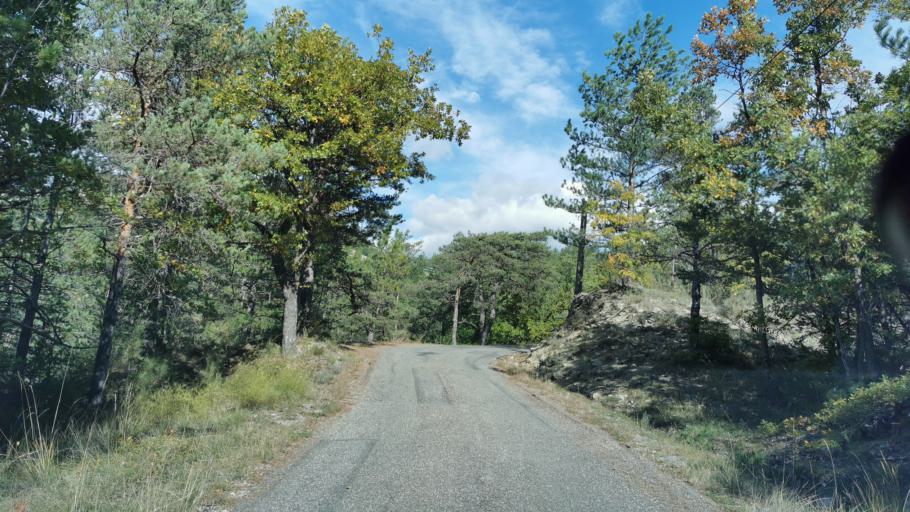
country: FR
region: Provence-Alpes-Cote d'Azur
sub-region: Departement des Alpes-de-Haute-Provence
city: Volonne
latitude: 44.1820
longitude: 6.0323
